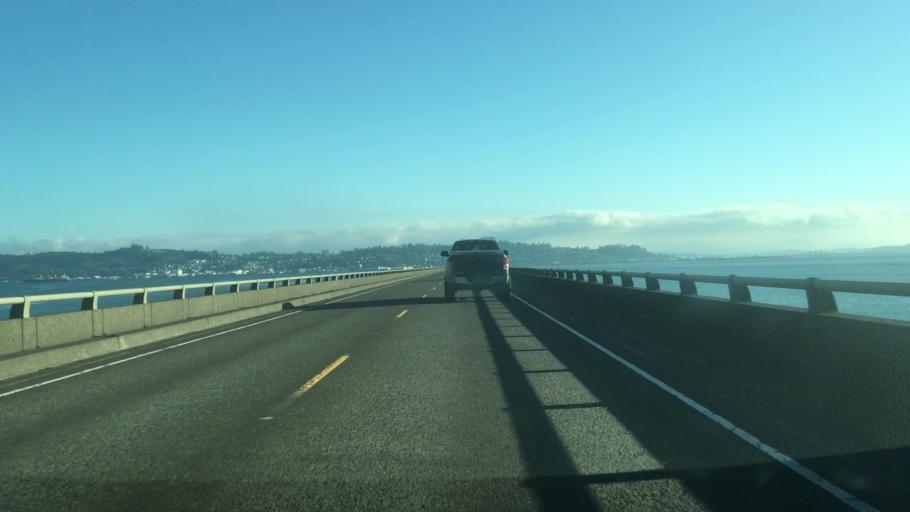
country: US
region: Oregon
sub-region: Clatsop County
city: Astoria
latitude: 46.2237
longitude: -123.8663
